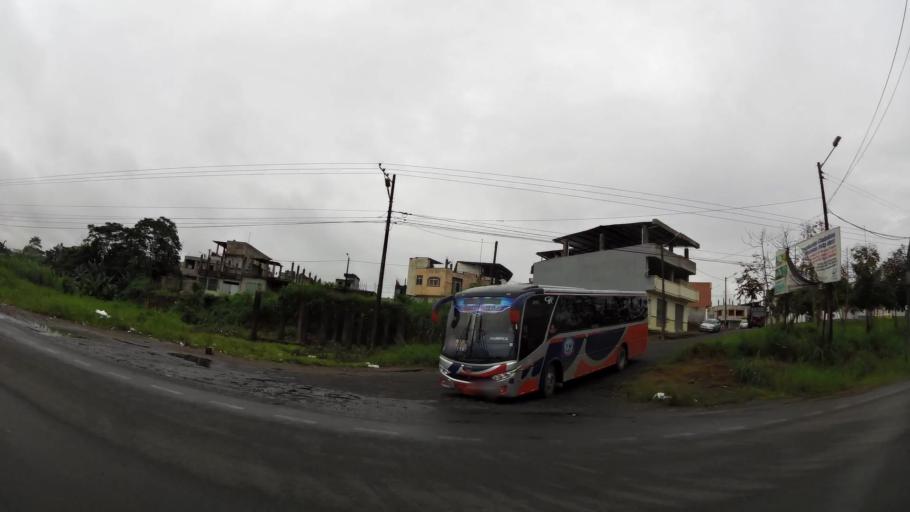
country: EC
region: Santo Domingo de los Tsachilas
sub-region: Canton Santo Domingo de los Colorados
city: Santo Domingo de los Colorados
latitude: -0.2387
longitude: -79.1833
